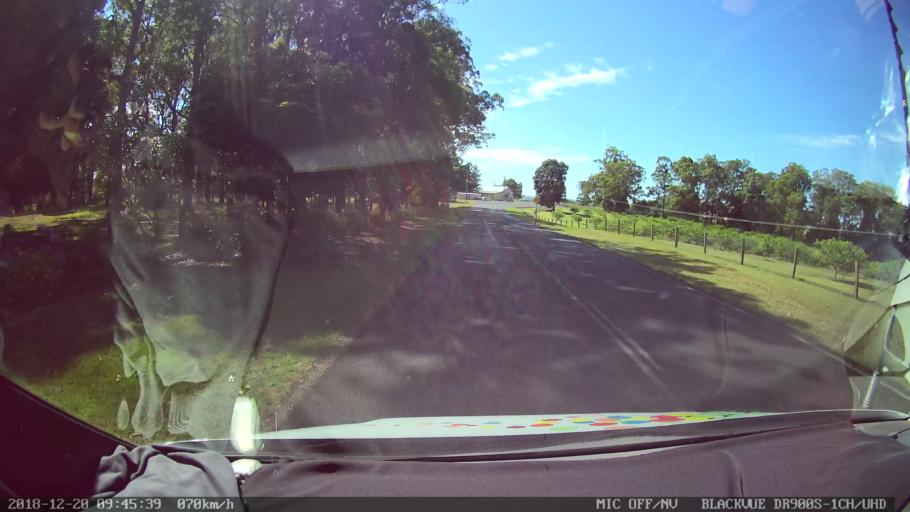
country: AU
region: New South Wales
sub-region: Lismore Municipality
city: Lismore
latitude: -28.7456
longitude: 153.3017
